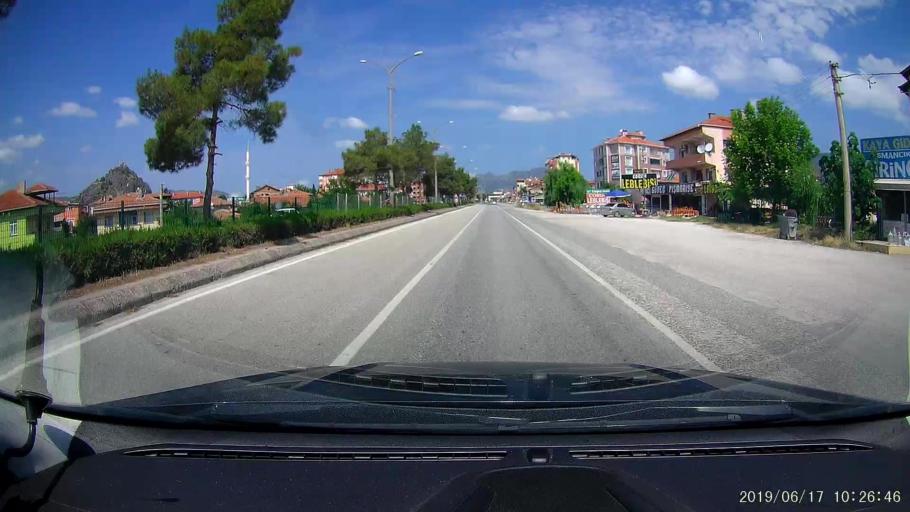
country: TR
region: Corum
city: Osmancik
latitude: 40.9752
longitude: 34.8149
